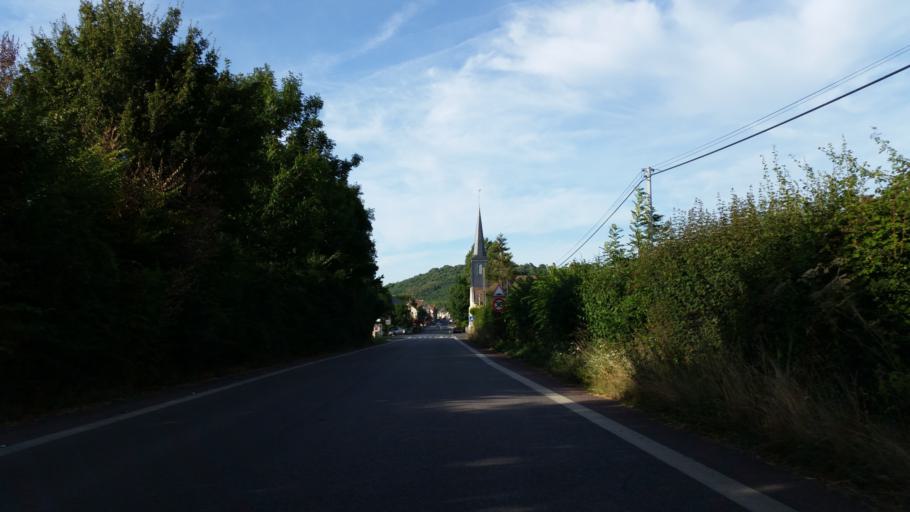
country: FR
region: Lower Normandy
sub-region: Departement du Calvados
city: Cambremer
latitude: 49.1137
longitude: 0.0106
